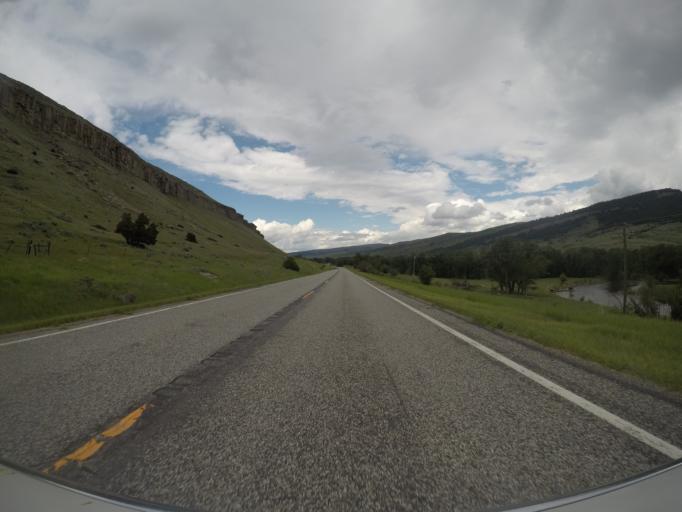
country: US
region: Montana
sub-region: Sweet Grass County
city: Big Timber
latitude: 45.5838
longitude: -110.1886
